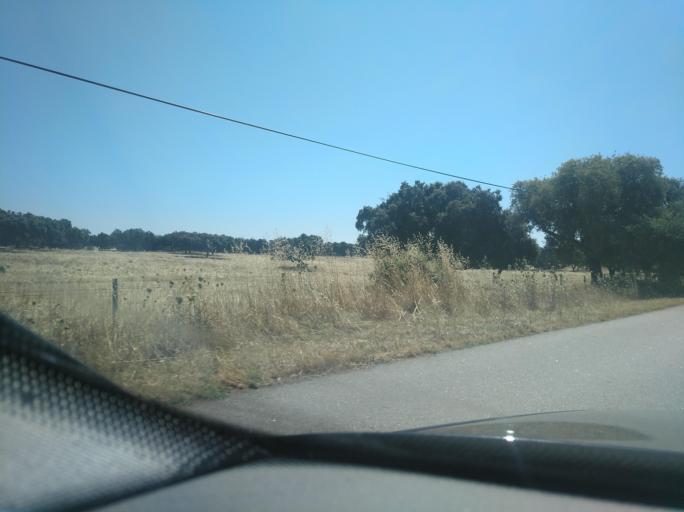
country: PT
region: Portalegre
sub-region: Arronches
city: Arronches
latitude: 38.9953
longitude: -7.3468
